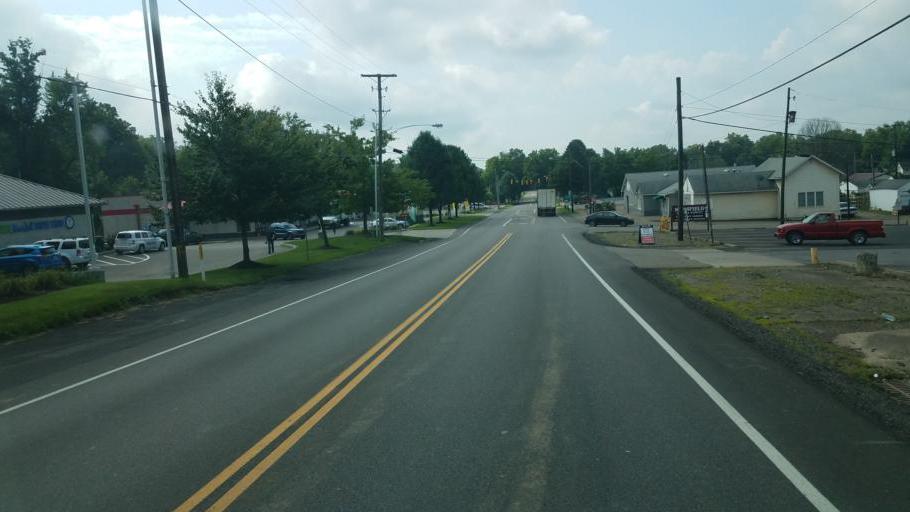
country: US
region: Ohio
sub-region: Knox County
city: Mount Vernon
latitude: 40.4067
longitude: -82.4935
